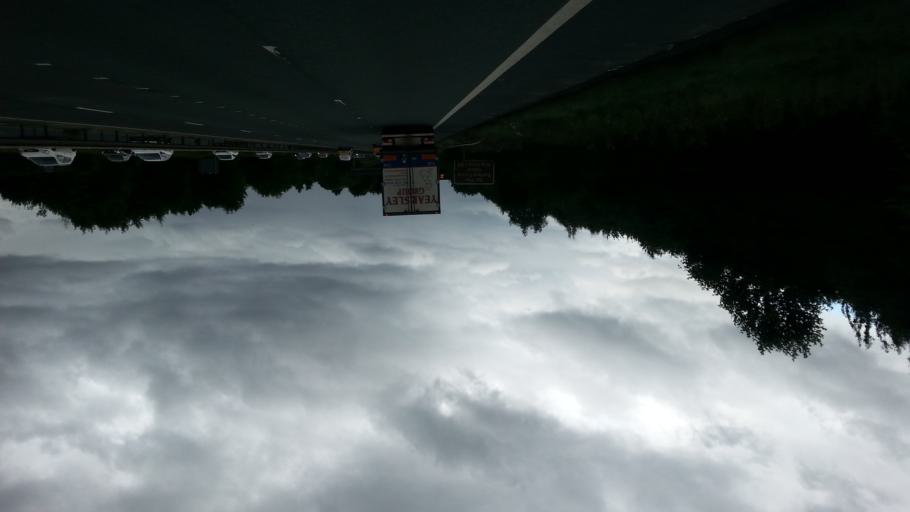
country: GB
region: England
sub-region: Borough of Bury
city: Prestwich
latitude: 53.5605
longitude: -2.2684
